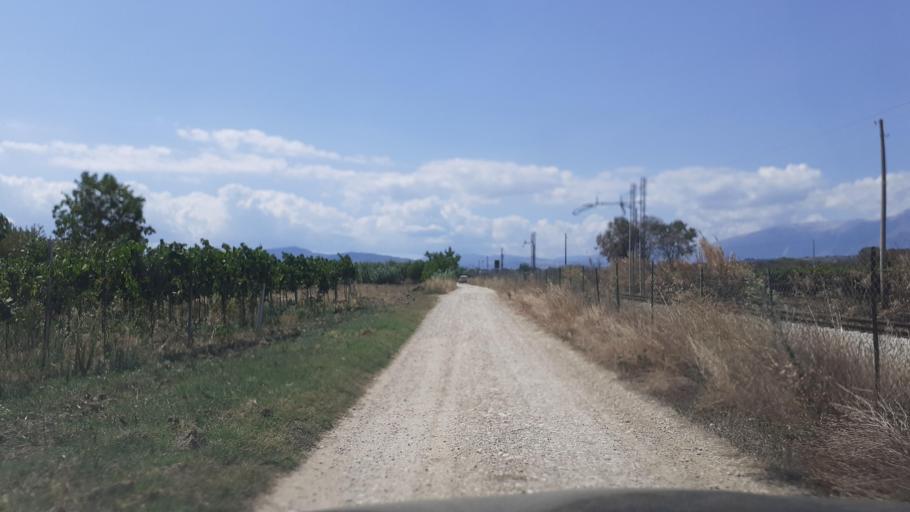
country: IT
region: Abruzzo
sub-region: Provincia di Chieti
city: Fossacesia
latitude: 42.2044
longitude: 14.4908
